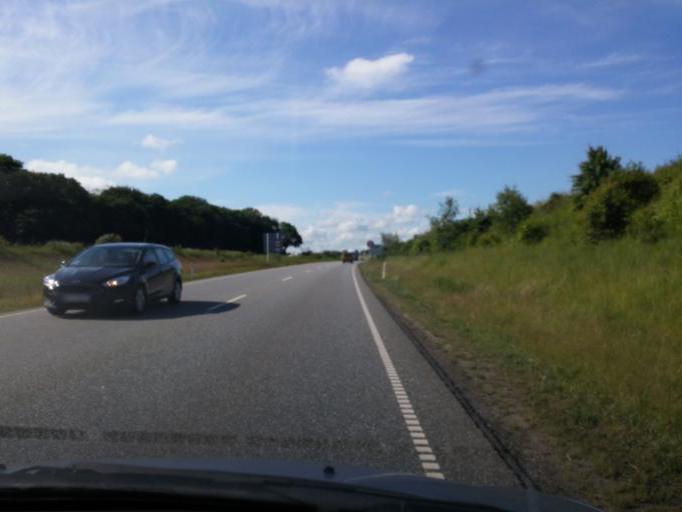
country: DK
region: South Denmark
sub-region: Odense Kommune
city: Neder Holluf
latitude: 55.3822
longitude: 10.4803
